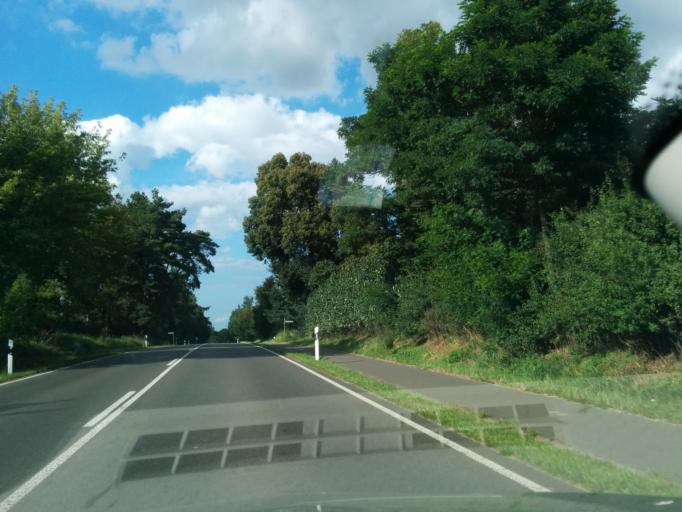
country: DE
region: Mecklenburg-Vorpommern
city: Pasewalk
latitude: 53.4823
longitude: 13.9830
